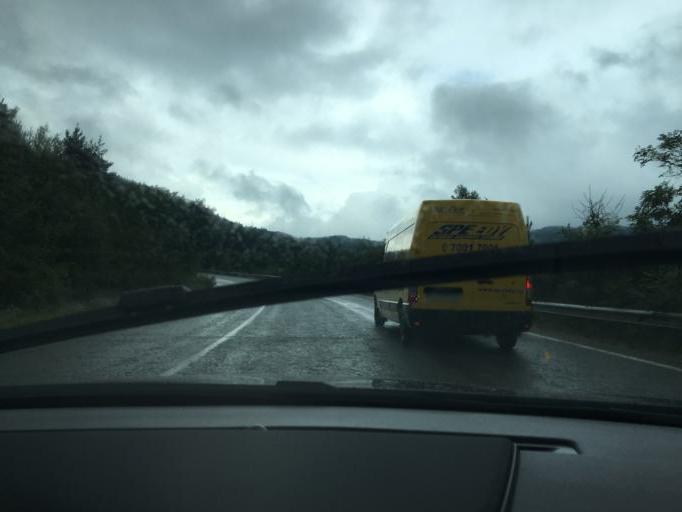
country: BG
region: Kyustendil
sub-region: Obshtina Kyustendil
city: Kyustendil
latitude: 42.2665
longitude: 22.5822
